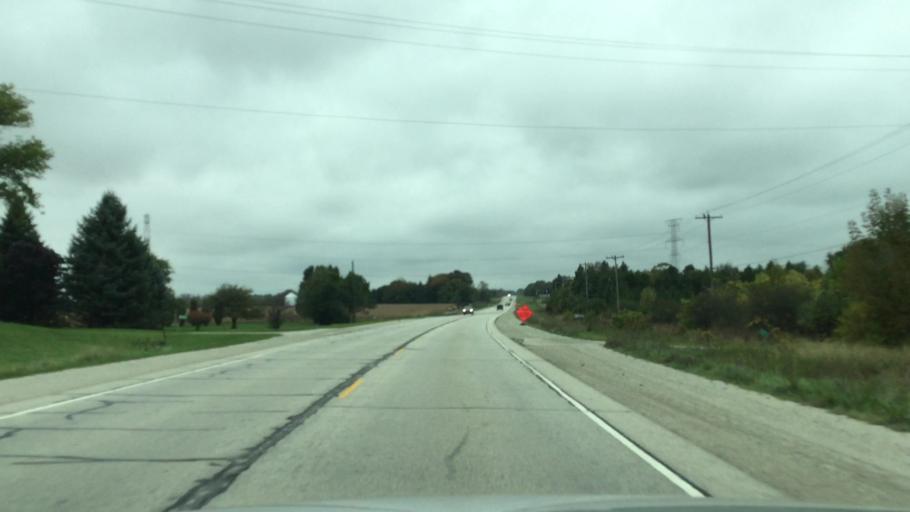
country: US
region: Wisconsin
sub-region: Racine County
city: Union Grove
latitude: 42.7334
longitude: -88.0076
